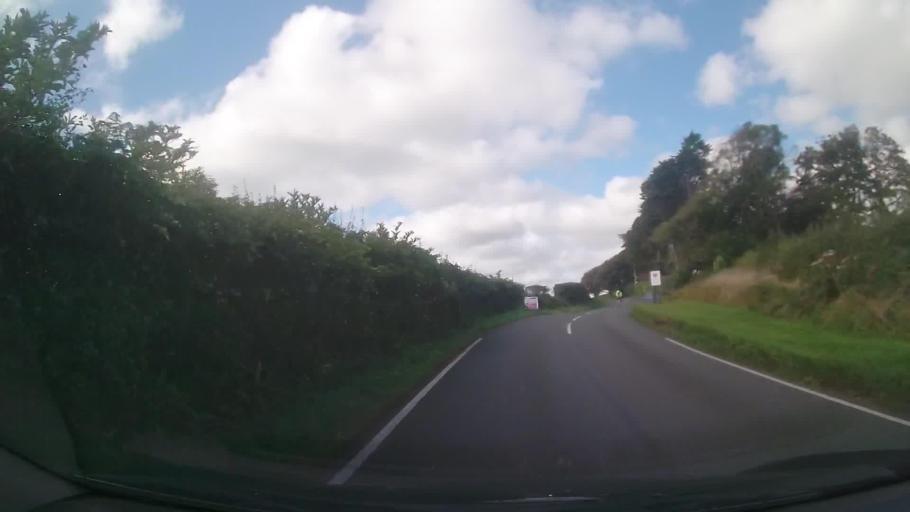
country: GB
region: Wales
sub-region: Pembrokeshire
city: Penally
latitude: 51.6568
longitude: -4.7488
